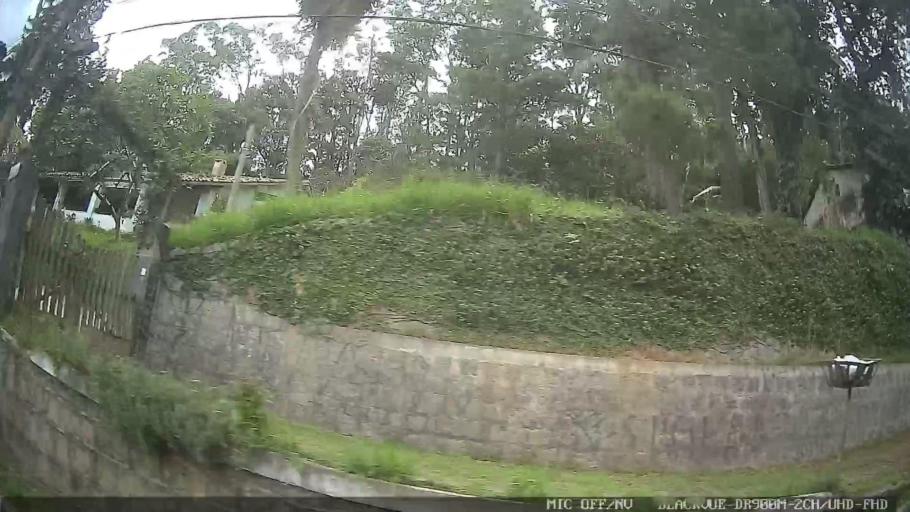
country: BR
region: Sao Paulo
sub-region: Ribeirao Pires
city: Ribeirao Pires
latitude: -23.7257
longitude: -46.4258
